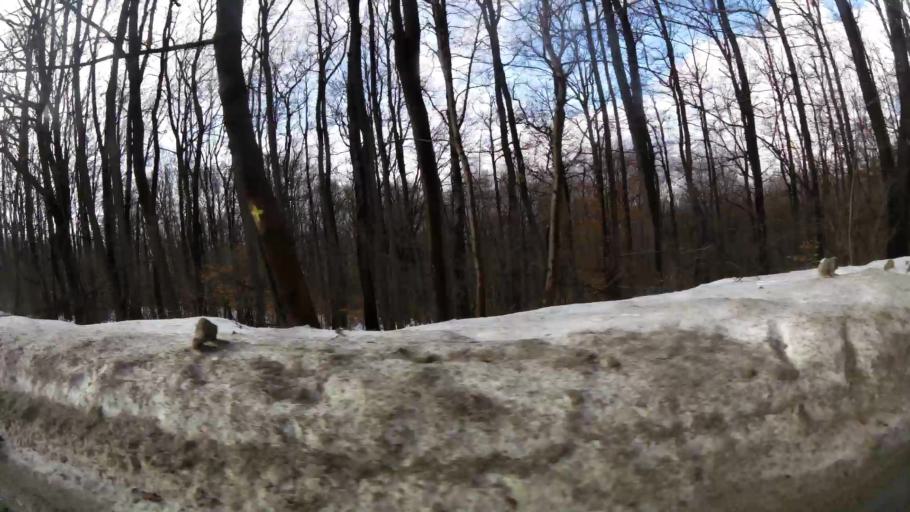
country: BG
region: Sofiya
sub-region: Obshtina Bozhurishte
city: Bozhurishte
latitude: 42.6408
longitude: 23.2164
